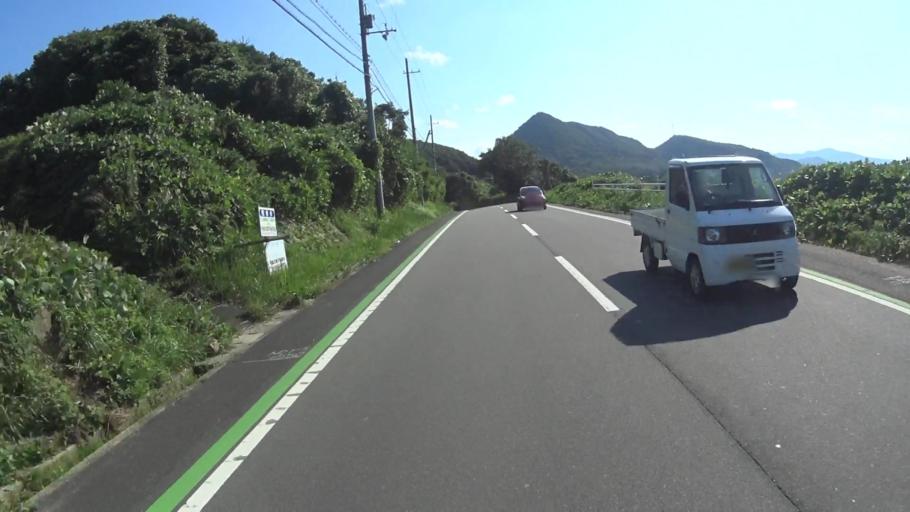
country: JP
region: Kyoto
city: Miyazu
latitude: 35.7268
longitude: 135.0864
